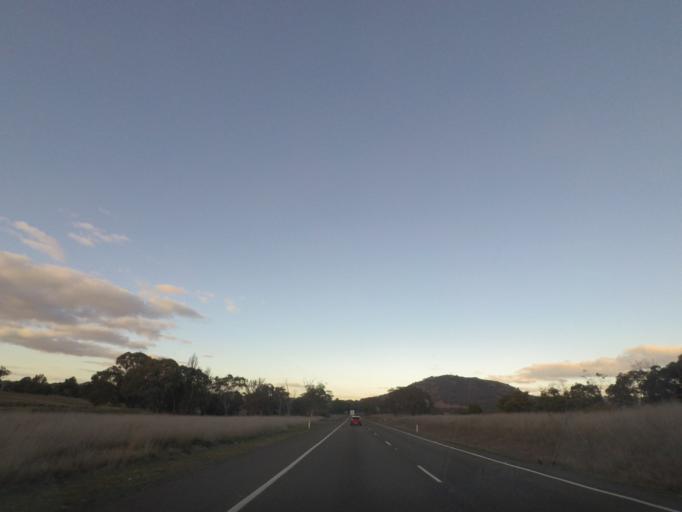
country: AU
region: New South Wales
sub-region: Yass Valley
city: Yass
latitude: -34.7704
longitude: 148.8004
